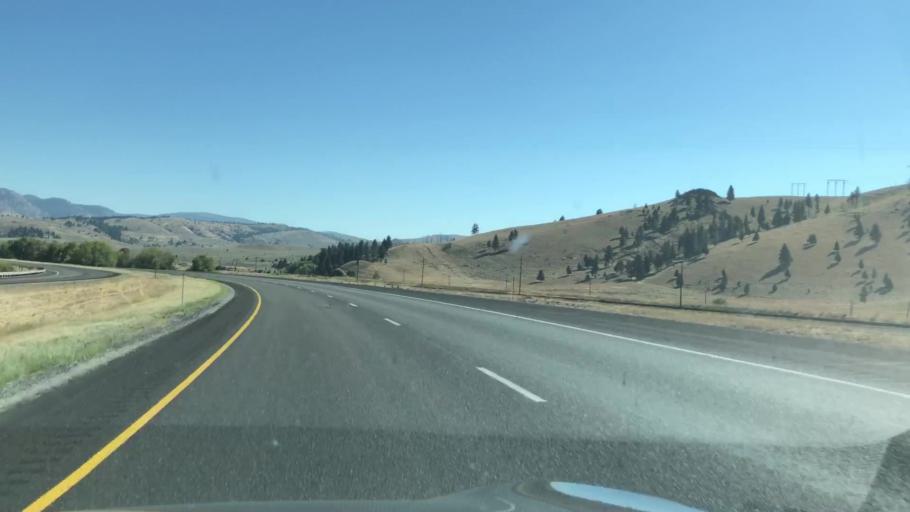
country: US
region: Montana
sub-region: Missoula County
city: Clinton
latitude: 46.6972
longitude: -113.3537
